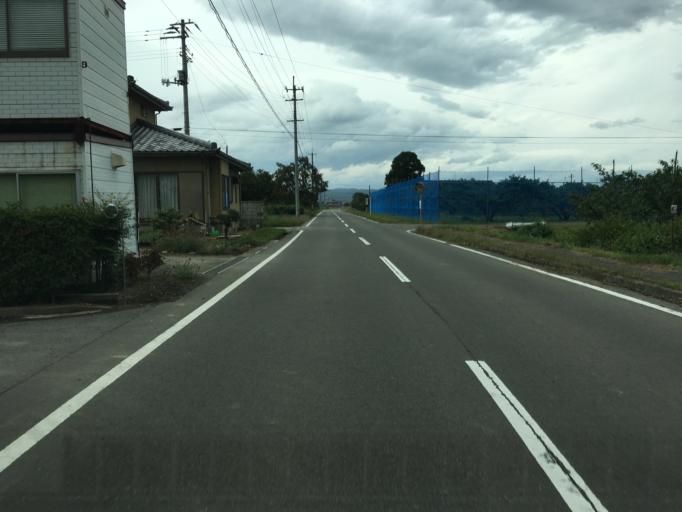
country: JP
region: Fukushima
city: Hobaramachi
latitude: 37.8380
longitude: 140.5661
